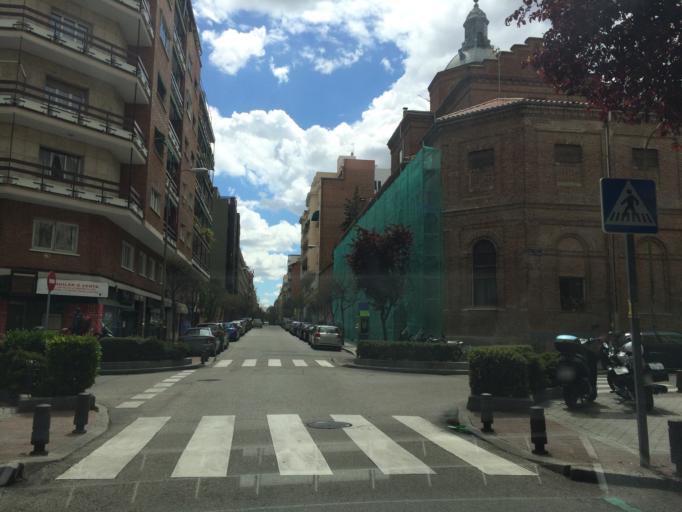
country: ES
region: Madrid
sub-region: Provincia de Madrid
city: Chamberi
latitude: 40.4443
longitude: -3.6989
